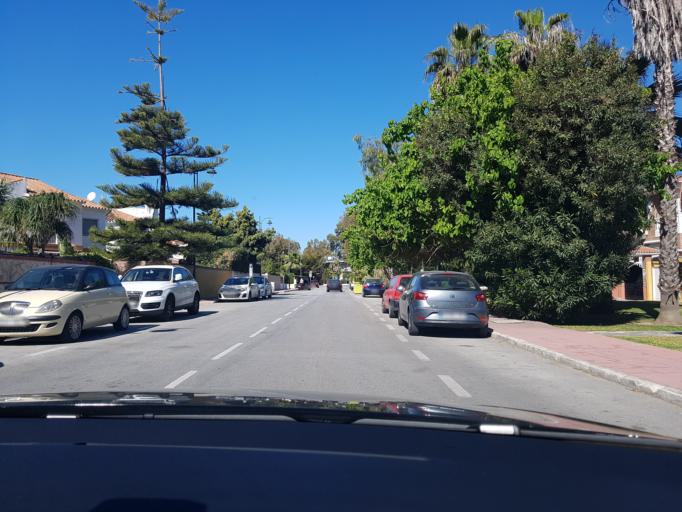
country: ES
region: Andalusia
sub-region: Provincia de Malaga
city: Torremolinos
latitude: 36.6683
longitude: -4.4635
